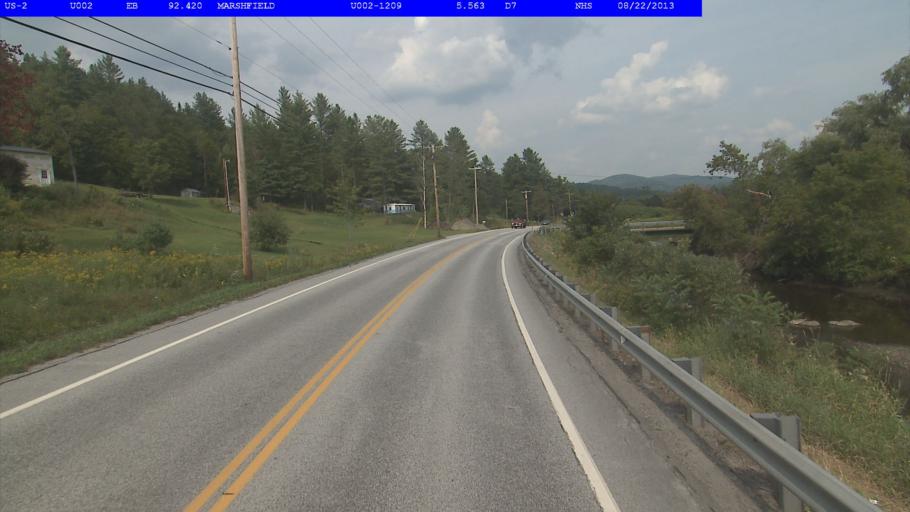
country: US
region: Vermont
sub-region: Caledonia County
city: Hardwick
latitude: 44.3432
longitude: -72.3684
